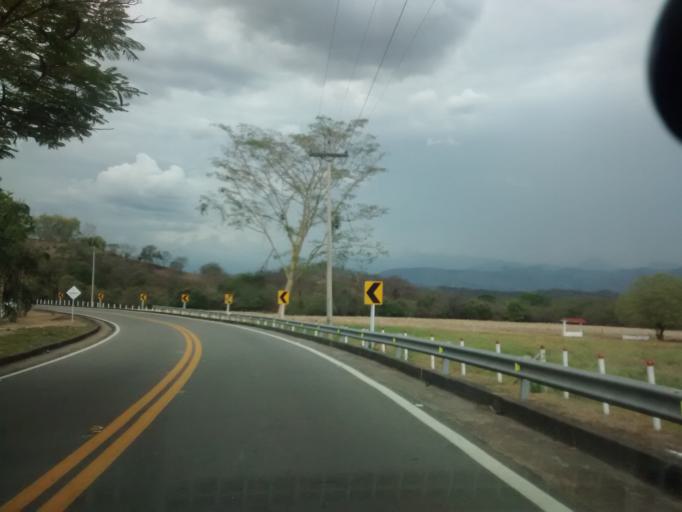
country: CO
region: Cundinamarca
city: Agua de Dios
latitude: 4.4094
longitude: -74.7106
